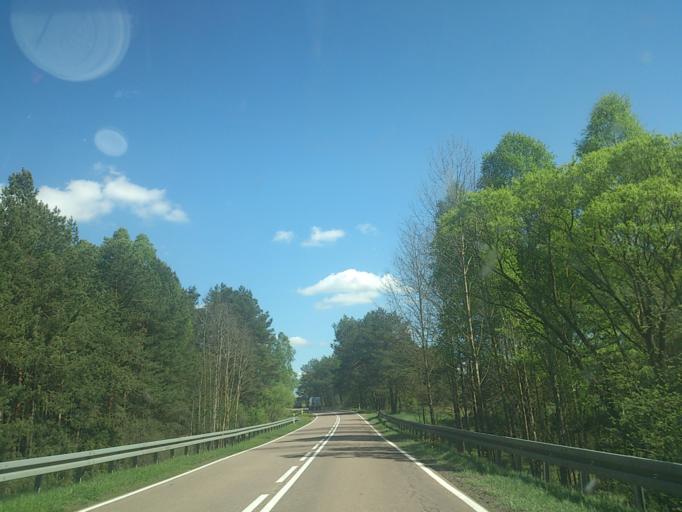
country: PL
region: Podlasie
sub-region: Powiat zambrowski
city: Rutki
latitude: 53.2042
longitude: 22.5400
